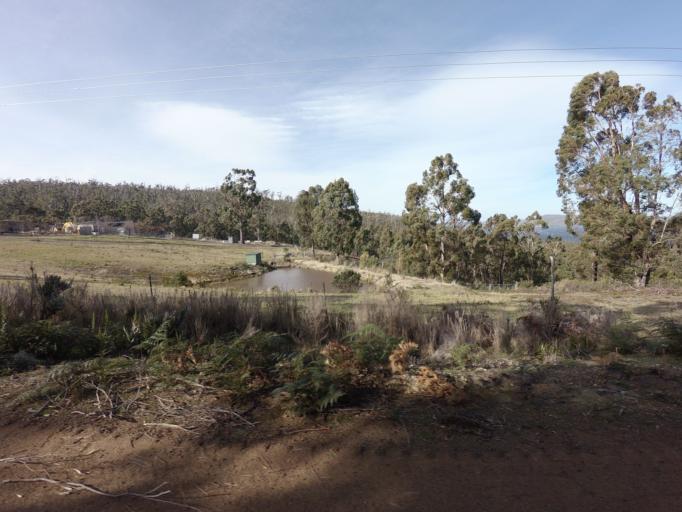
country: AU
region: Tasmania
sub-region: Kingborough
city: Kettering
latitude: -43.0935
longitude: 147.2640
